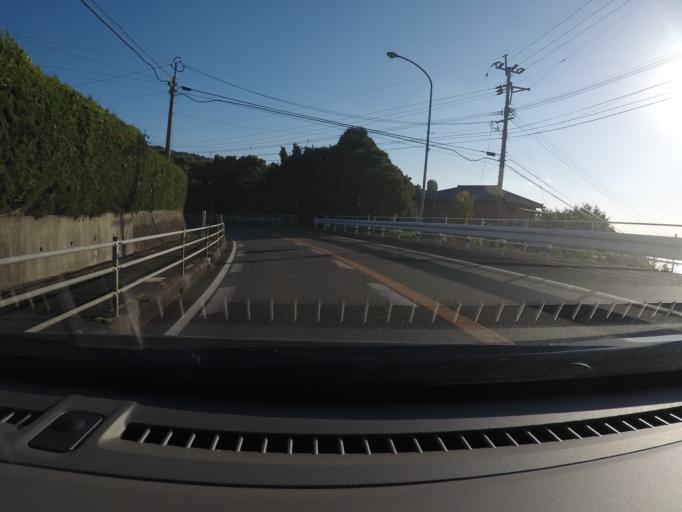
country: JP
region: Kumamoto
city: Minamata
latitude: 32.1561
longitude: 130.3634
